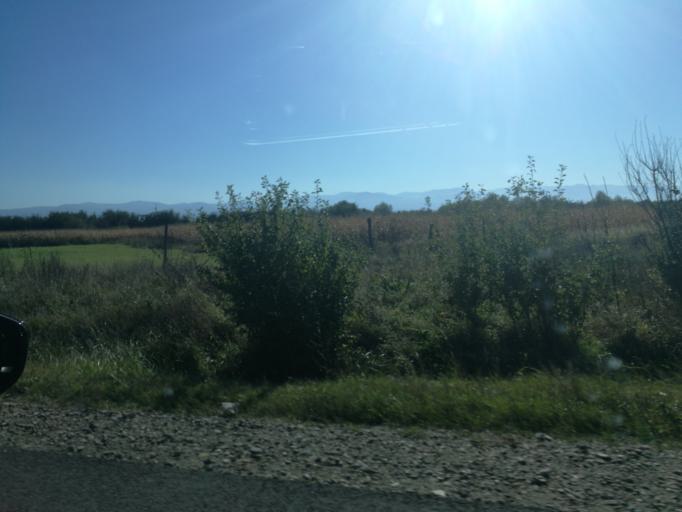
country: RO
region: Brasov
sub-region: Comuna Sercaia
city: Sercaia
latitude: 45.8273
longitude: 25.1513
